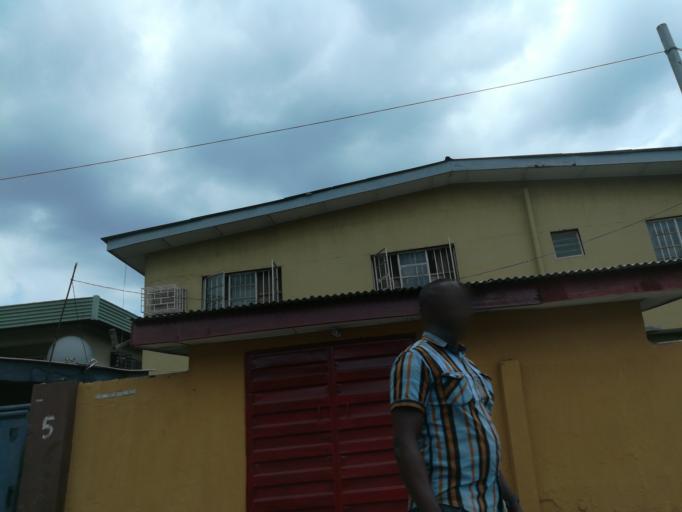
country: NG
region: Lagos
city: Ikeja
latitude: 6.5940
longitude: 3.3561
